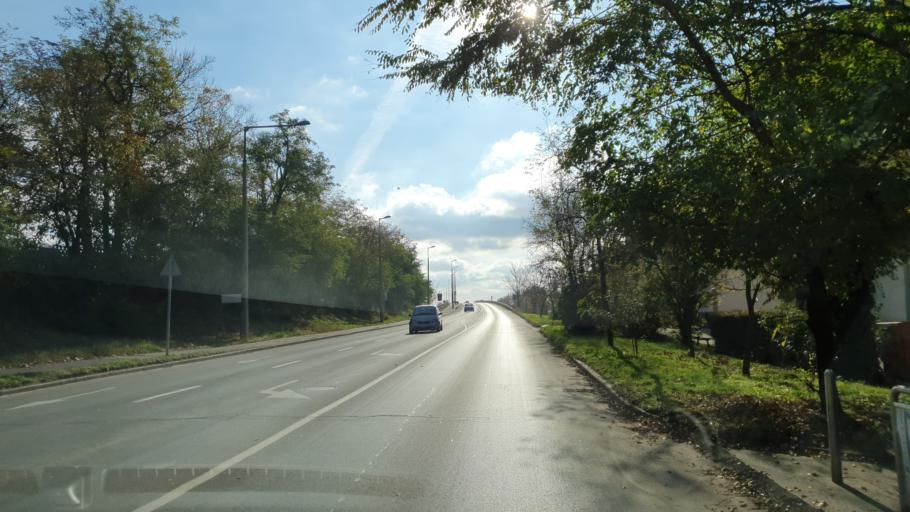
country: HU
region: Szabolcs-Szatmar-Bereg
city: Kisvarda
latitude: 48.2158
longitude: 22.0834
